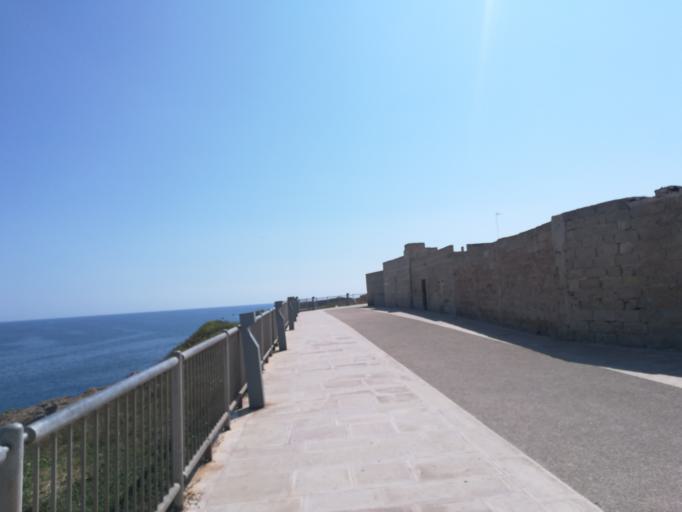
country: IT
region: Apulia
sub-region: Provincia di Bari
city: Polignano a Mare
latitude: 40.9961
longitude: 17.2254
